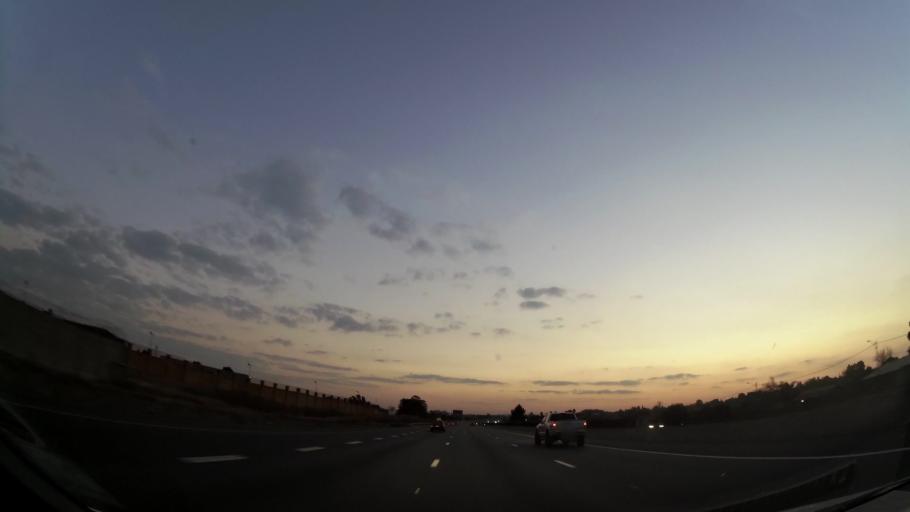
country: ZA
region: Gauteng
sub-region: Ekurhuleni Metropolitan Municipality
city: Germiston
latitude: -26.2570
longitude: 28.1835
